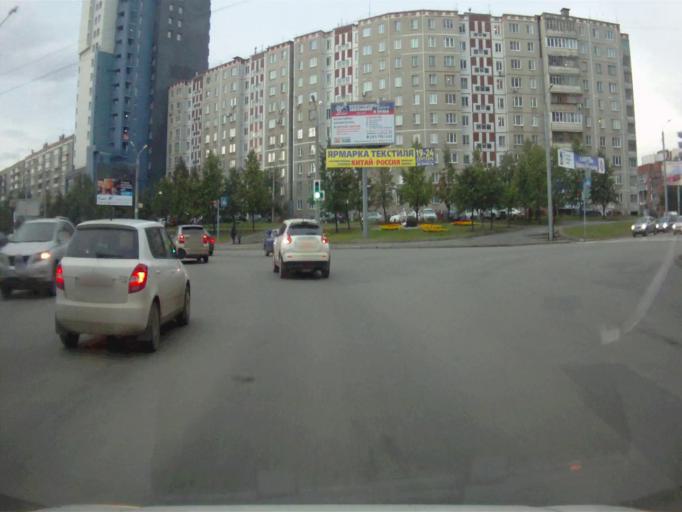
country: RU
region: Chelyabinsk
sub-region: Gorod Chelyabinsk
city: Chelyabinsk
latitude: 55.1534
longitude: 61.3816
